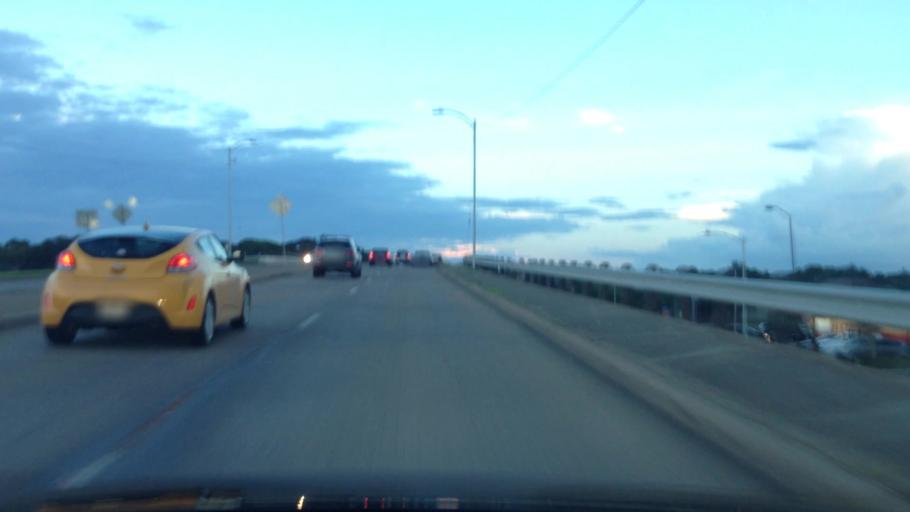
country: US
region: Texas
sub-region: Tarrant County
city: Arlington
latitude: 32.7376
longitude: -97.1318
